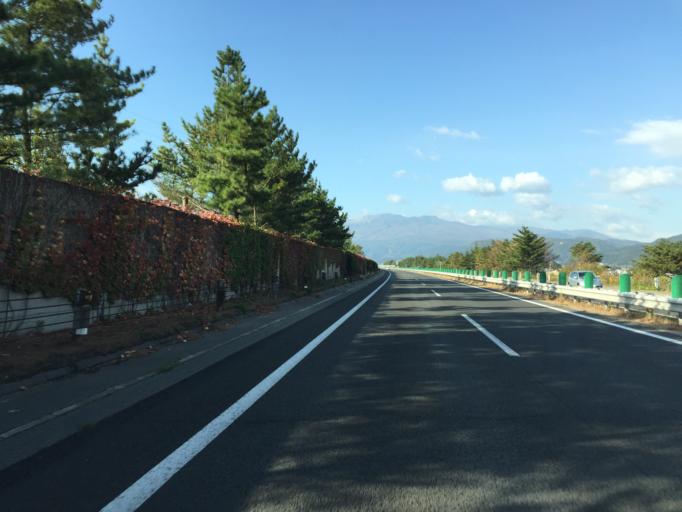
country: JP
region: Fukushima
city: Fukushima-shi
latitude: 37.7994
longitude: 140.4370
